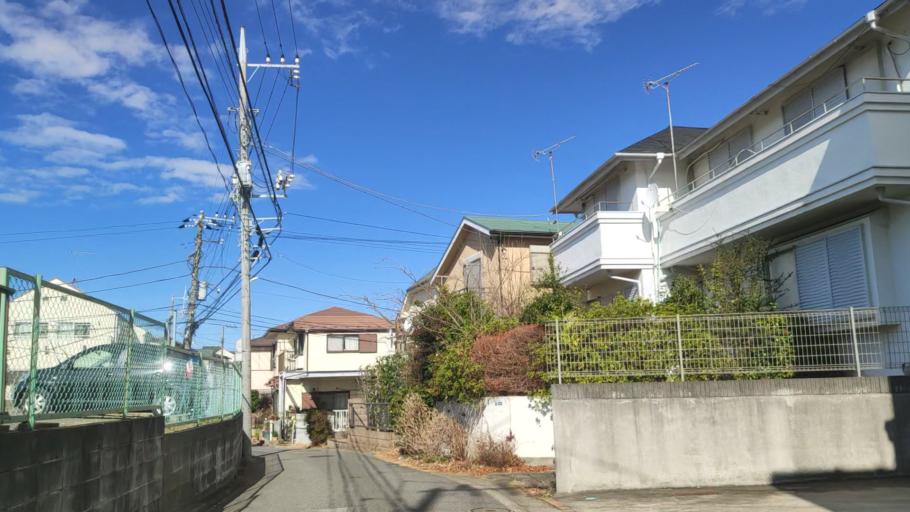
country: JP
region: Kanagawa
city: Yokohama
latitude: 35.4722
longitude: 139.5822
